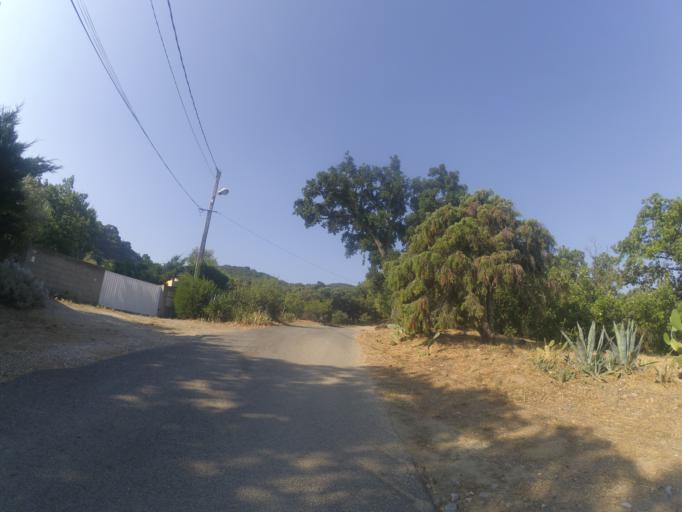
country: FR
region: Languedoc-Roussillon
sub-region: Departement des Pyrenees-Orientales
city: Ille-sur-Tet
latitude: 42.6530
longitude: 2.6568
